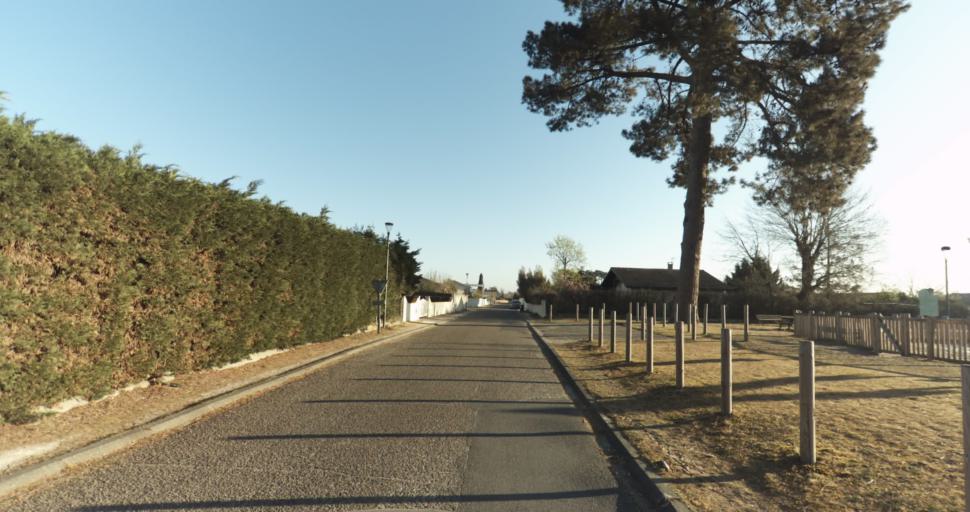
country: FR
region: Aquitaine
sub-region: Departement de la Gironde
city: Martignas-sur-Jalle
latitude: 44.8125
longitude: -0.7815
